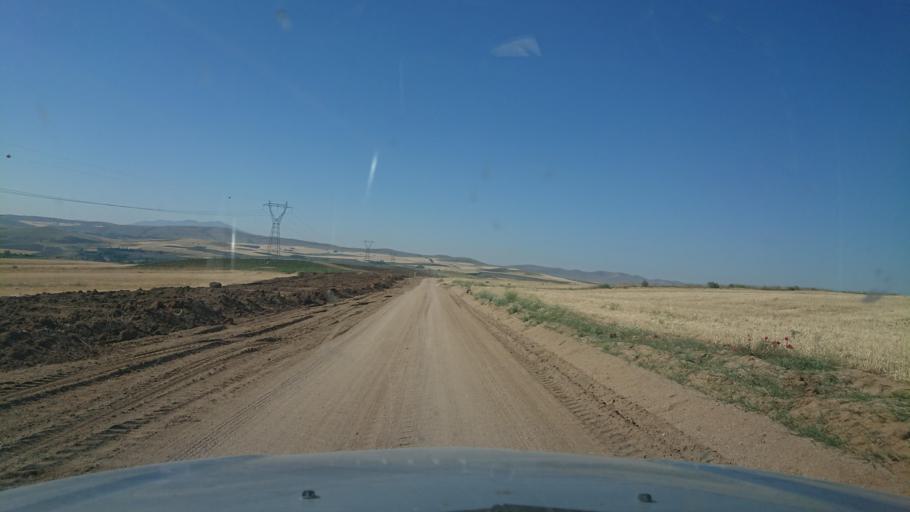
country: TR
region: Aksaray
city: Agacoren
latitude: 38.8394
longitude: 33.9443
